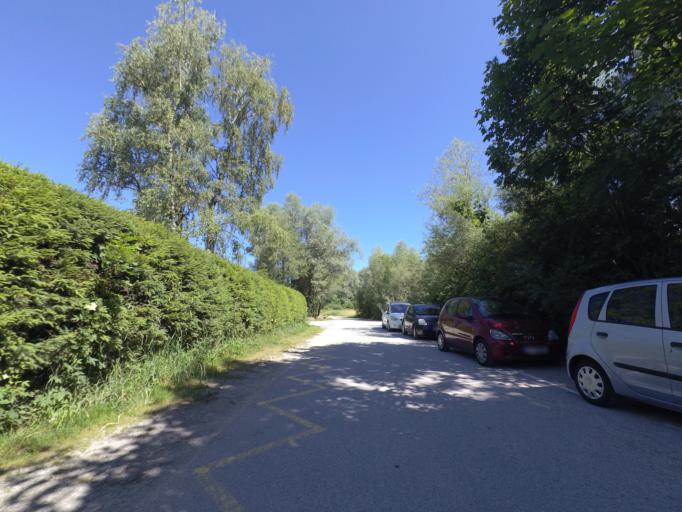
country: AT
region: Salzburg
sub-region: Politischer Bezirk Salzburg-Umgebung
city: Anif
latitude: 47.7308
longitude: 13.0695
